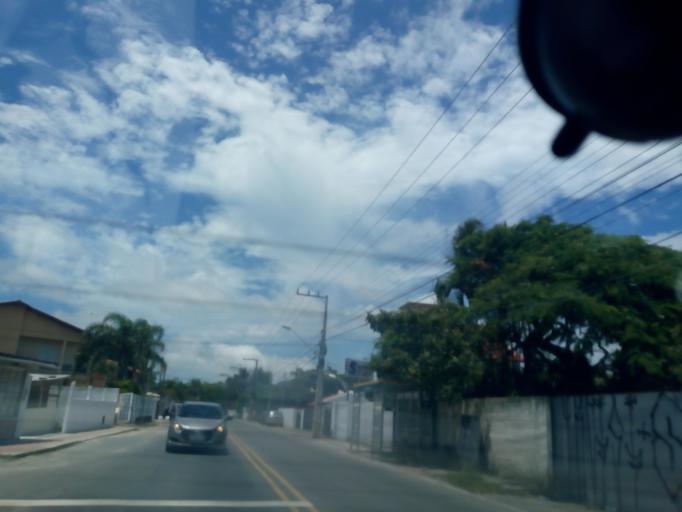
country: BR
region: Santa Catarina
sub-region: Florianopolis
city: Itacorubi
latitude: -27.4038
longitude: -48.4268
